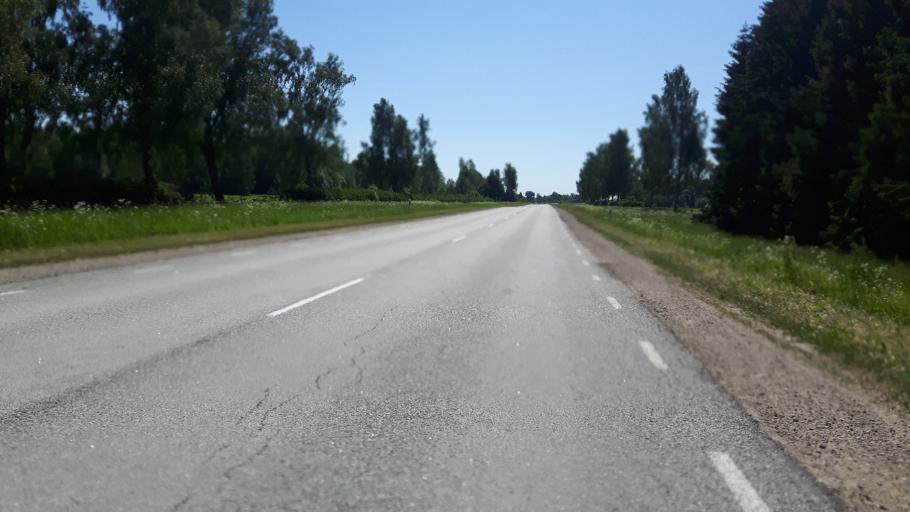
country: EE
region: Paernumaa
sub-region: Tootsi vald
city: Tootsi
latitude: 58.4583
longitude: 24.7800
